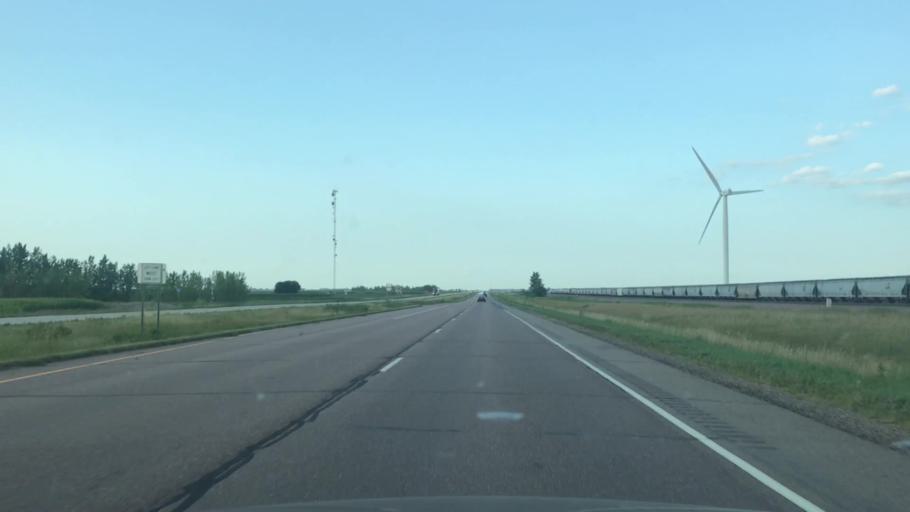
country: US
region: Minnesota
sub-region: Nobles County
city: Worthington
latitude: 43.7156
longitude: -95.4453
